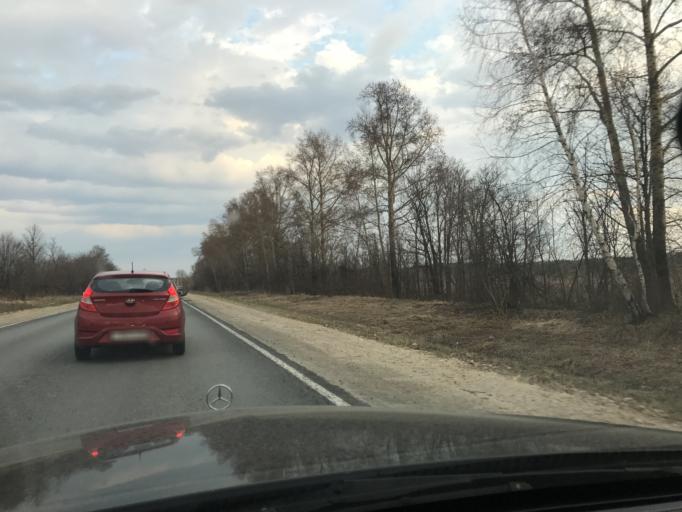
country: RU
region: Vladimir
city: Murom
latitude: 55.6420
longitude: 41.8463
